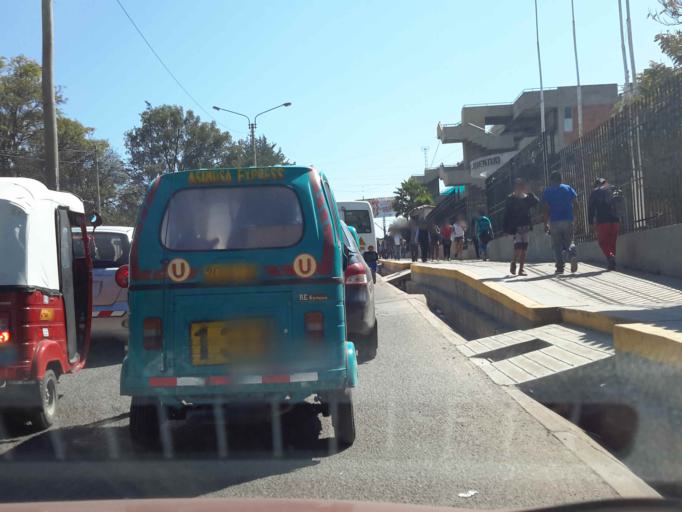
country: PE
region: Ayacucho
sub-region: Provincia de Huamanga
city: Ayacucho
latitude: -13.1547
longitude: -74.2238
